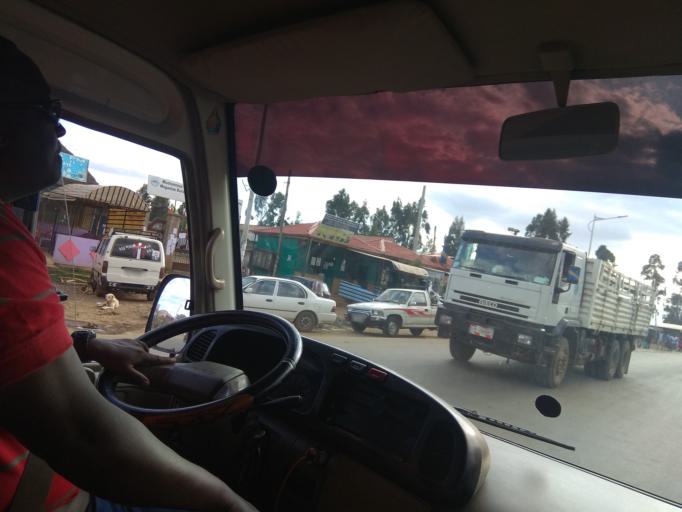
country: ET
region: Adis Abeba
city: Addis Ababa
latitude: 9.0257
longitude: 38.6538
